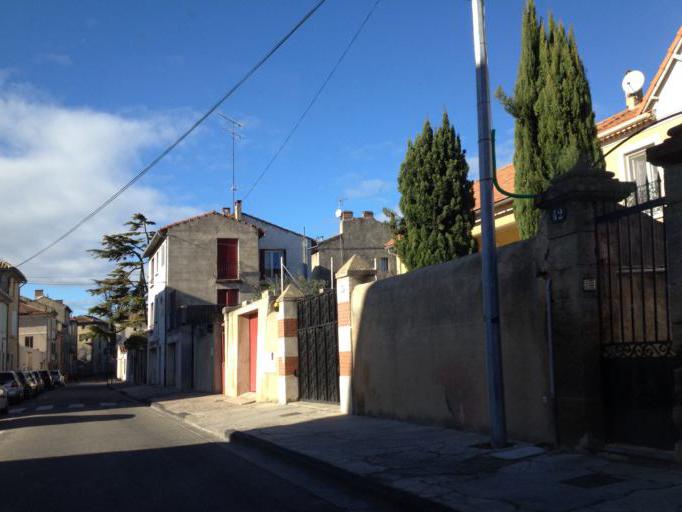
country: FR
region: Provence-Alpes-Cote d'Azur
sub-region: Departement du Vaucluse
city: Orange
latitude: 44.1385
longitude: 4.8111
